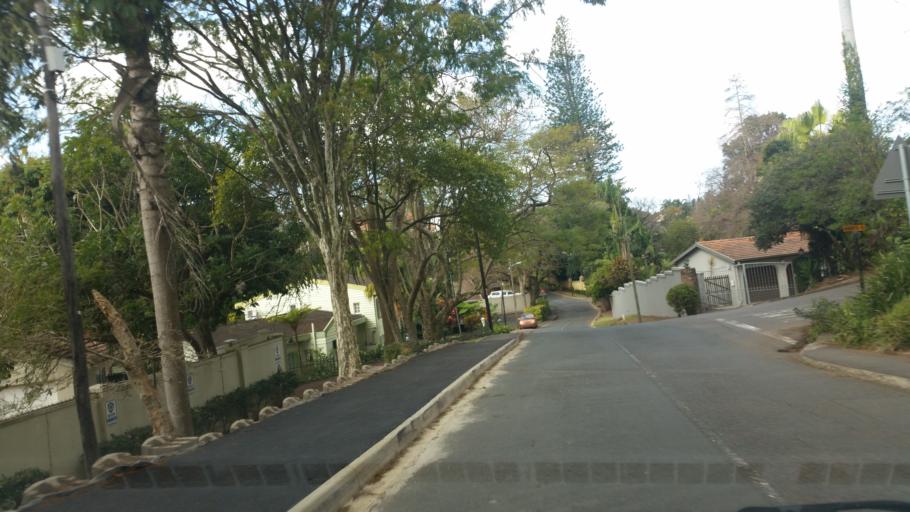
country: ZA
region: KwaZulu-Natal
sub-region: eThekwini Metropolitan Municipality
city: Berea
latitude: -29.8292
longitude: 30.9302
